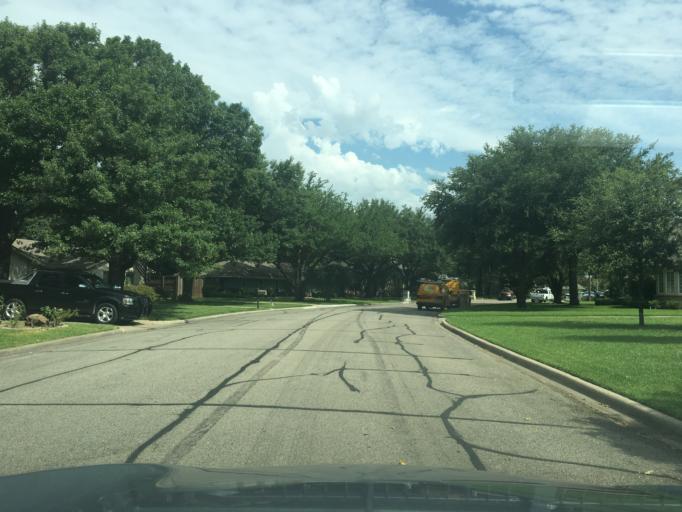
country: US
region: Texas
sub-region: Dallas County
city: Farmers Branch
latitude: 32.9285
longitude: -96.8613
